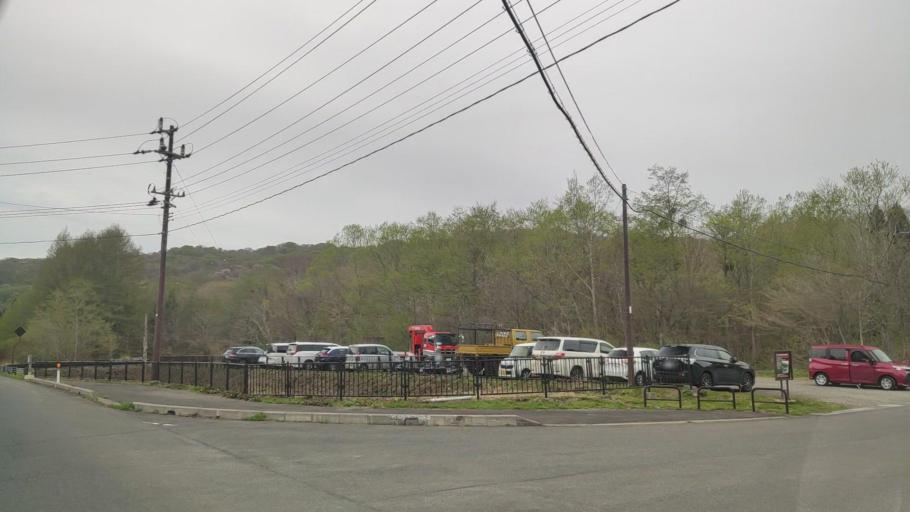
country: JP
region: Akita
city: Hanawa
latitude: 40.4433
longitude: 140.9319
